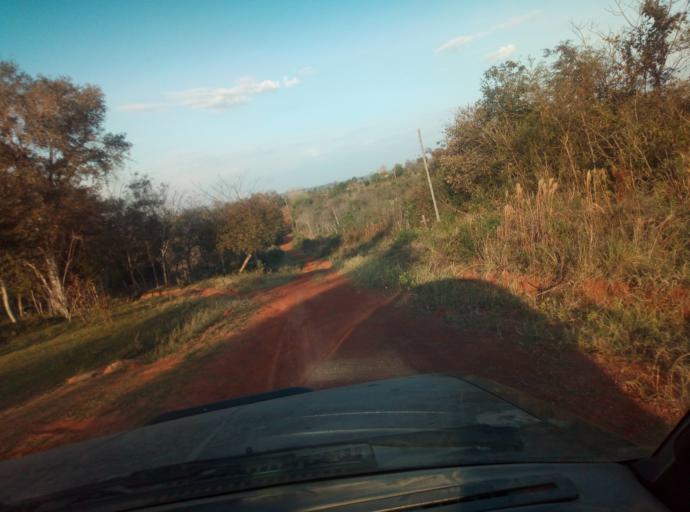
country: PY
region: Caaguazu
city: Doctor Cecilio Baez
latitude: -25.1530
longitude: -56.2398
